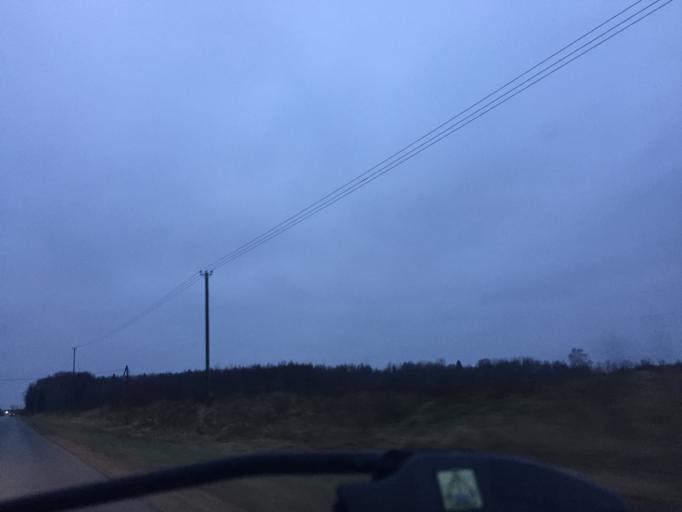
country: LV
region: Limbazu Rajons
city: Limbazi
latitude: 57.5978
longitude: 24.7977
